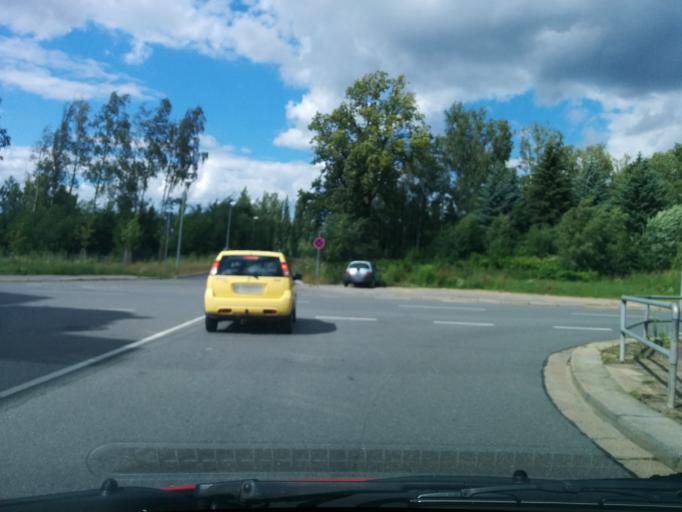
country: DE
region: Saxony
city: Hilbersdorf
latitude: 50.8382
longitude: 12.9570
